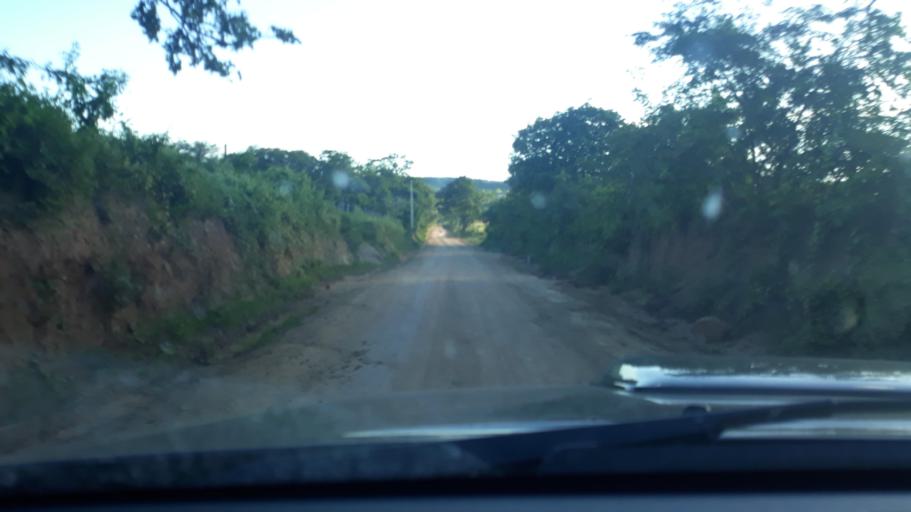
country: BR
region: Bahia
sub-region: Riacho De Santana
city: Riacho de Santana
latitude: -13.8207
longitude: -42.7243
